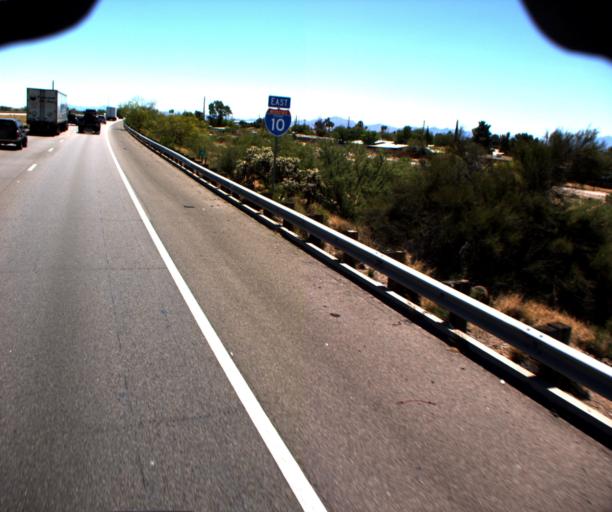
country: US
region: Arizona
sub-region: Pima County
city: Tucson
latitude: 32.1523
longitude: -110.9005
